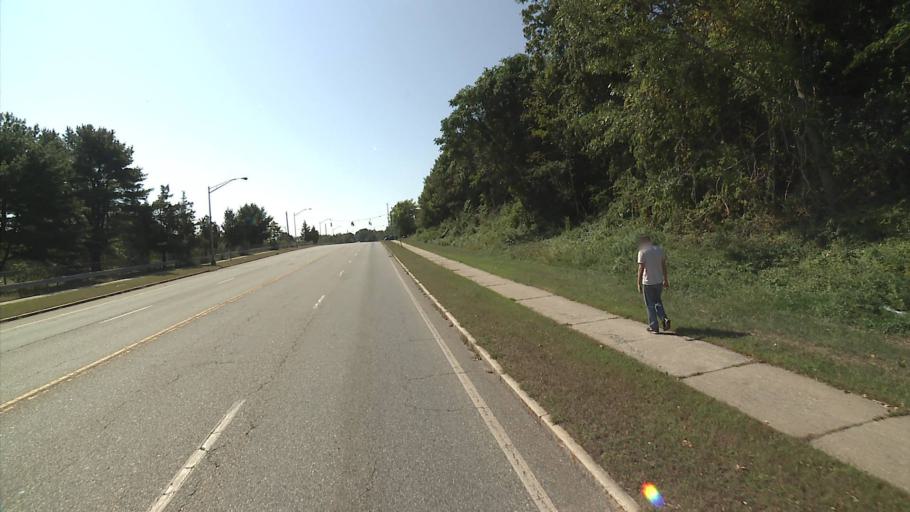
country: US
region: Connecticut
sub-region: New London County
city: New London
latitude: 41.3690
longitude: -72.1071
